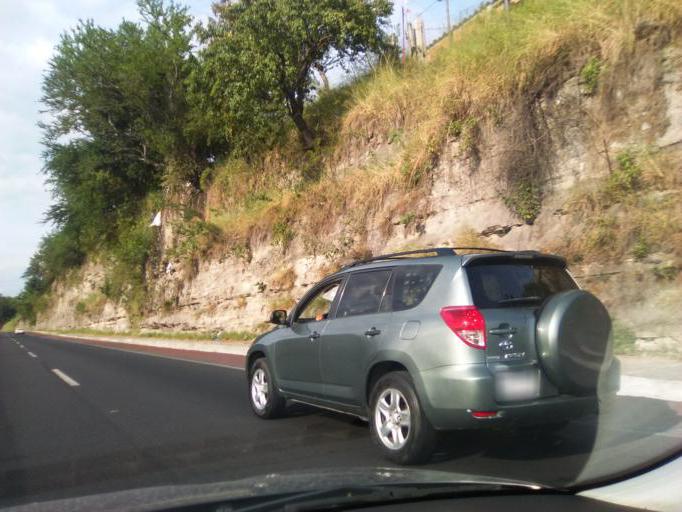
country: MX
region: Morelos
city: Temixco
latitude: 18.8699
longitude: -99.2252
